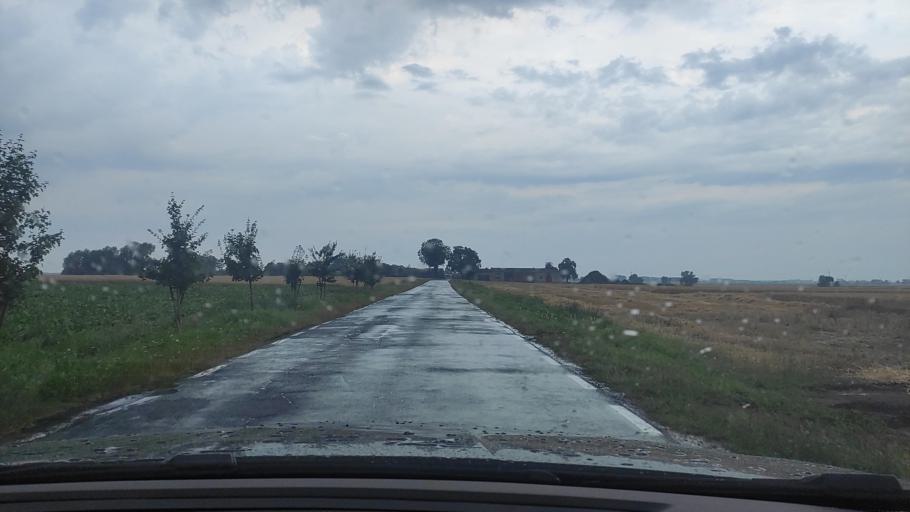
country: PL
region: Greater Poland Voivodeship
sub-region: Powiat poznanski
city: Kleszczewo
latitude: 52.2929
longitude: 17.1685
